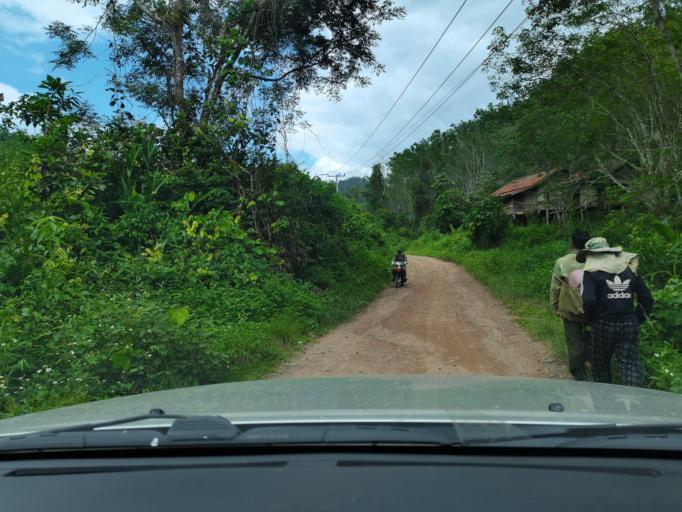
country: LA
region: Loungnamtha
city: Muang Long
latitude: 20.7011
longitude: 101.0317
